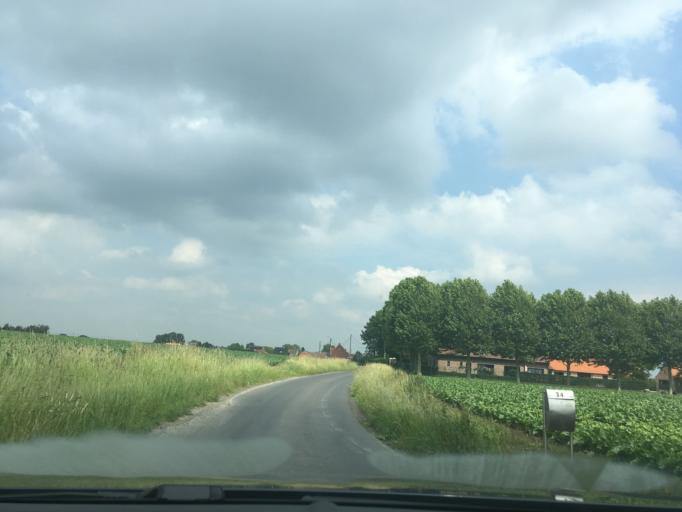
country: BE
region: Flanders
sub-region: Provincie West-Vlaanderen
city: Meulebeke
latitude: 50.9466
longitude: 3.3053
